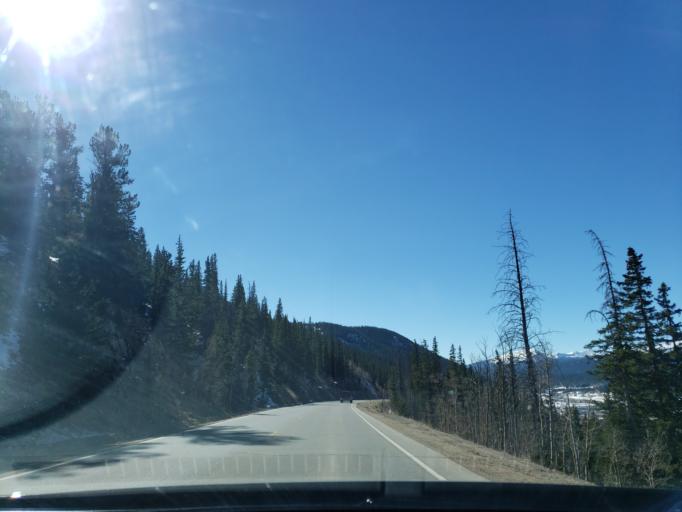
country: US
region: Colorado
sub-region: Park County
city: Fairplay
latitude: 39.3304
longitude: -106.0520
